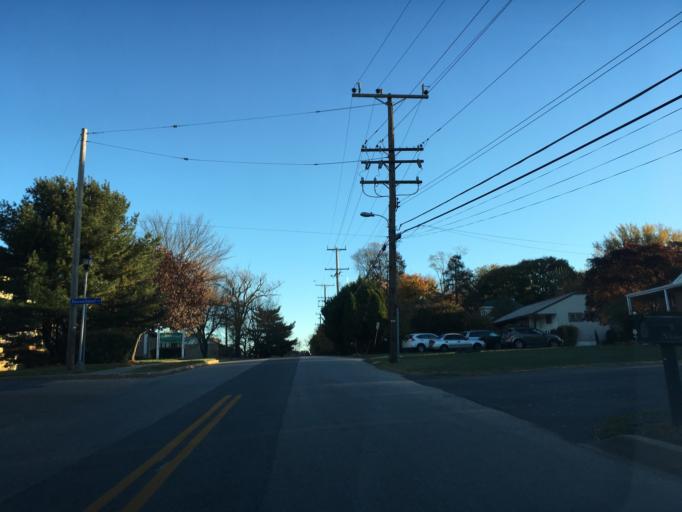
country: US
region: Maryland
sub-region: Baltimore County
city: Owings Mills
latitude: 39.4178
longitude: -76.7753
